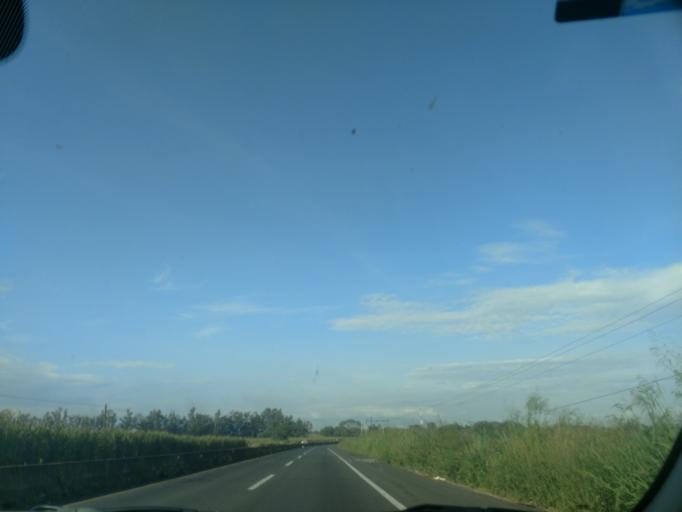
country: MX
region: Jalisco
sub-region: Ameca
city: Los Pocitos
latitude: 20.5391
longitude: -103.9245
